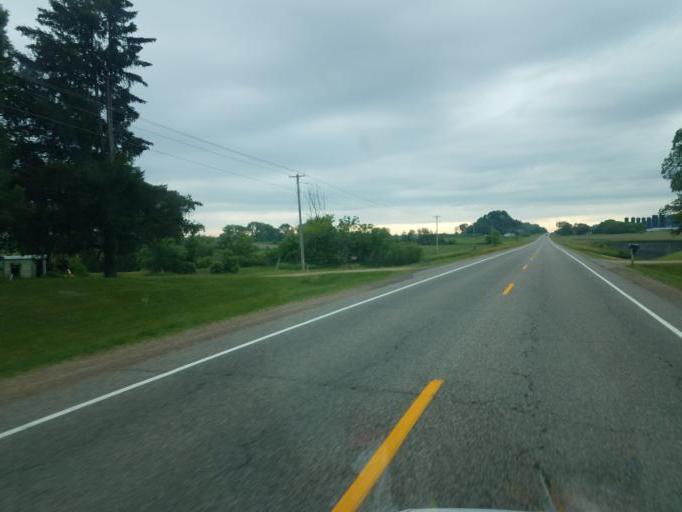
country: US
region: Wisconsin
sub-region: Juneau County
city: Mauston
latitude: 43.7891
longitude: -90.1514
